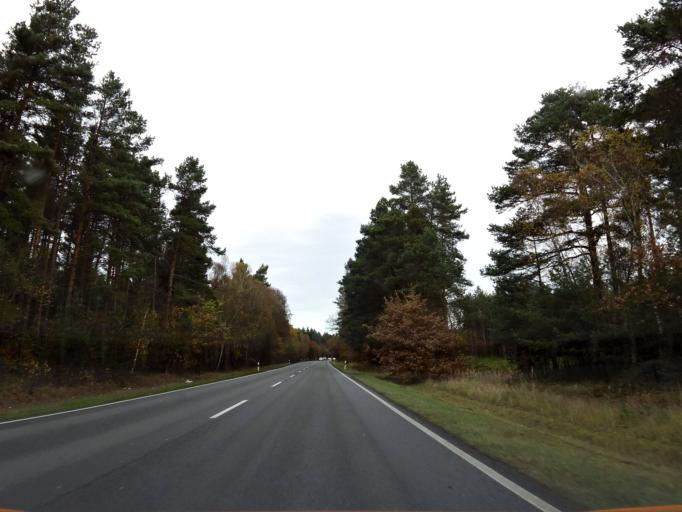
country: DE
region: Saxony-Anhalt
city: Haldensleben I
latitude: 52.3523
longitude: 11.4511
